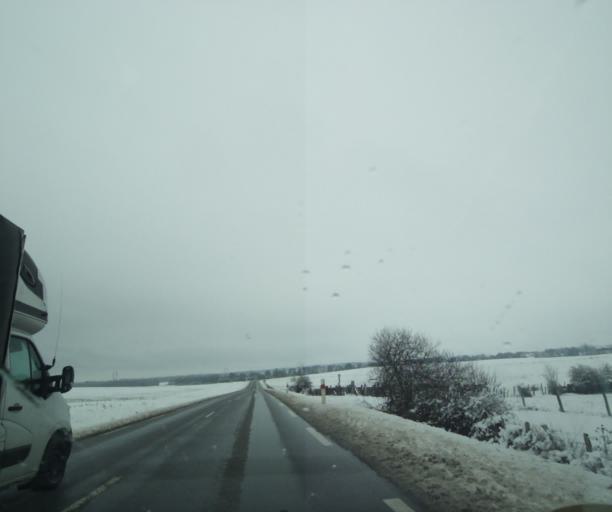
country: FR
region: Champagne-Ardenne
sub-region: Departement de la Haute-Marne
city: Montier-en-Der
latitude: 48.5146
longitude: 4.8061
